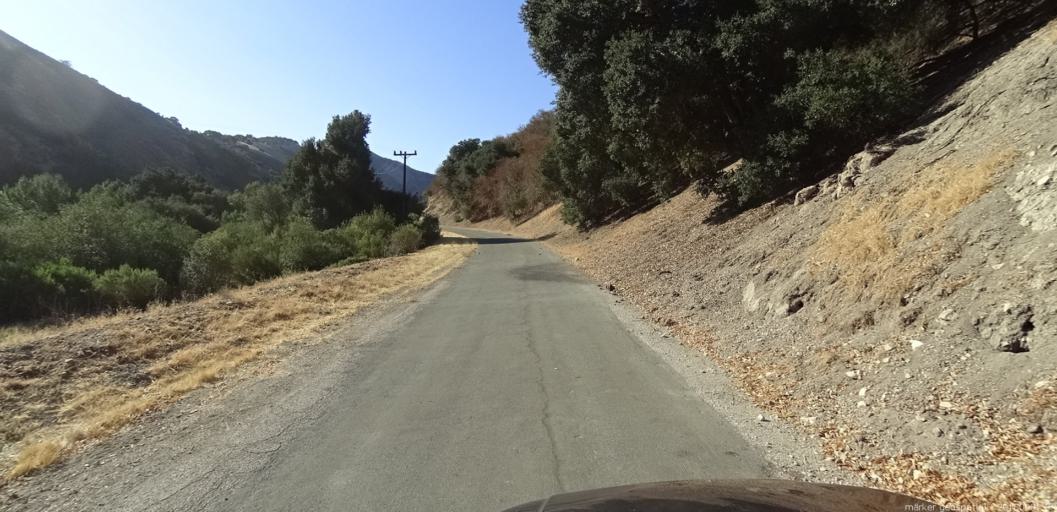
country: US
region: California
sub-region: Monterey County
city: Greenfield
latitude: 36.2139
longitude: -121.2807
